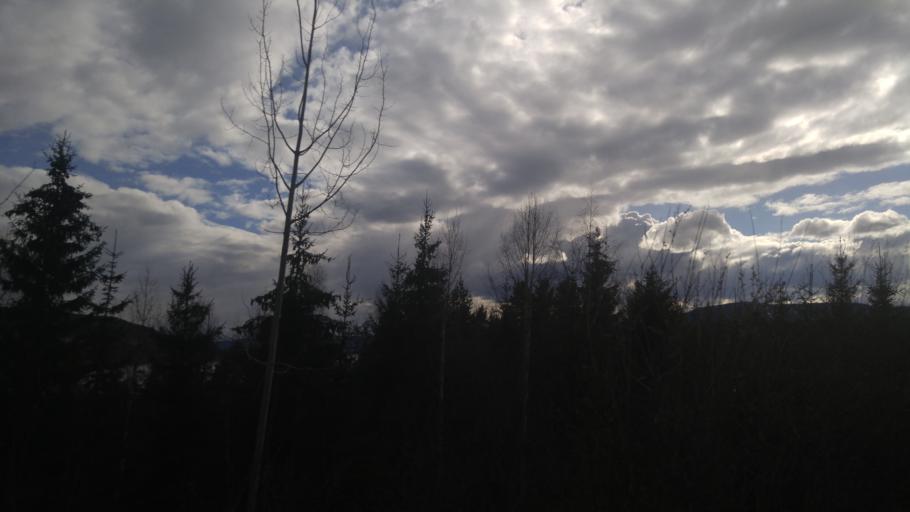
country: NO
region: Hedmark
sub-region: Stange
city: Stange
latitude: 60.6045
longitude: 11.2864
